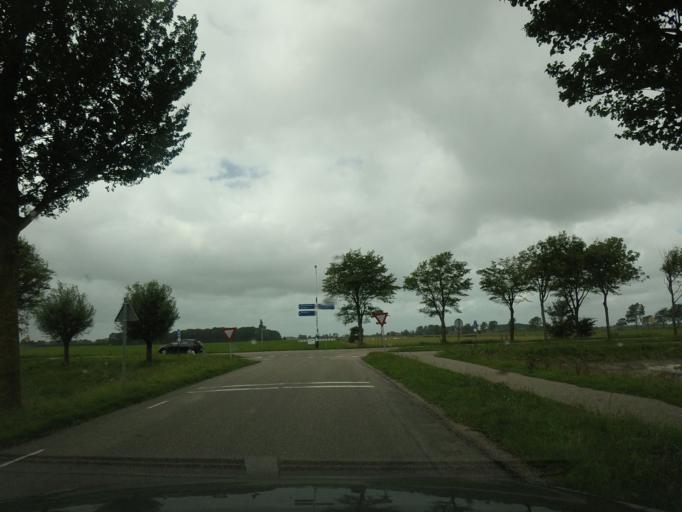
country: NL
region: North Holland
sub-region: Gemeente Schagen
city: Harenkarspel
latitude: 52.7360
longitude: 4.7395
